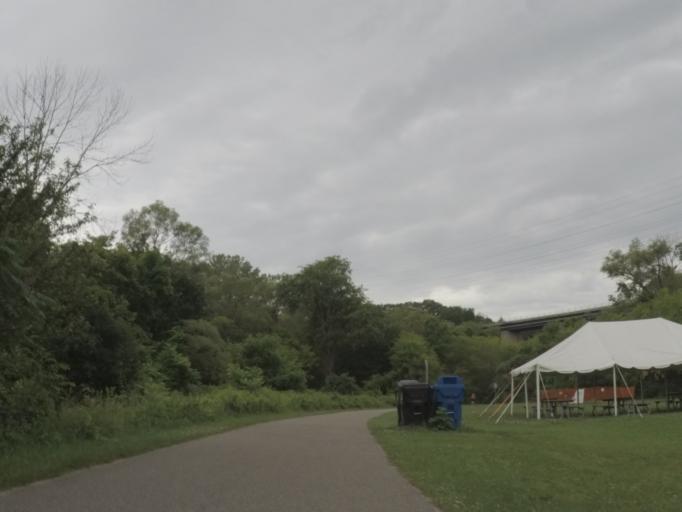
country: CA
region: Ontario
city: Etobicoke
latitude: 43.6625
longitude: -79.5095
